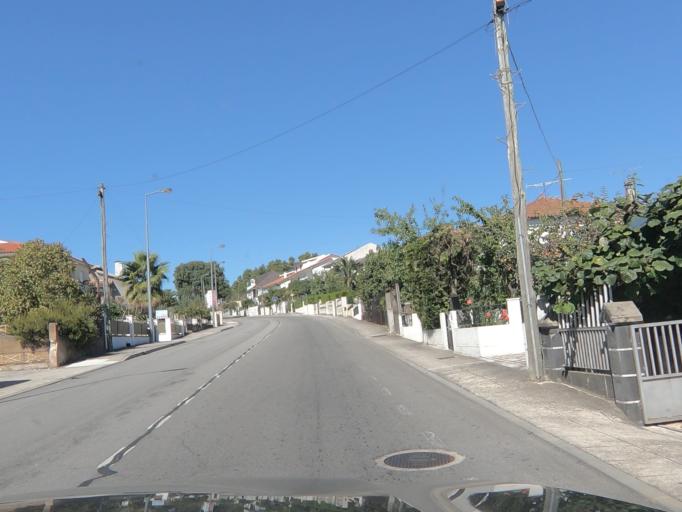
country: PT
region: Vila Real
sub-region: Valpacos
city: Valpacos
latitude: 41.6172
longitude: -7.3104
